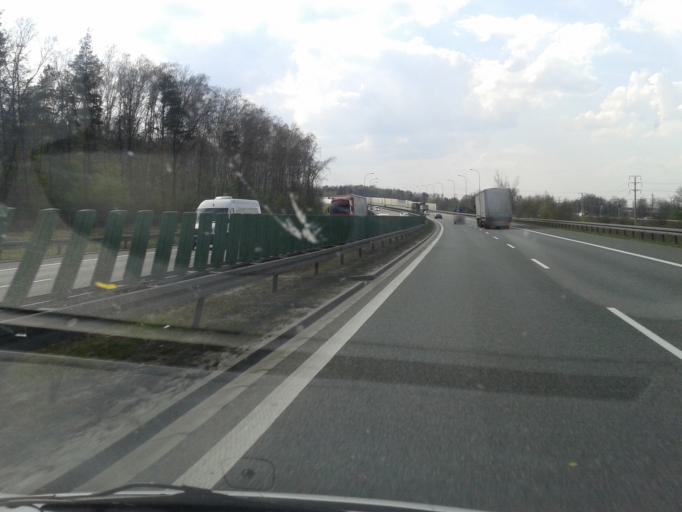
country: PL
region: Lesser Poland Voivodeship
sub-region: Powiat wielicki
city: Kokotow
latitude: 50.0176
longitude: 20.0773
